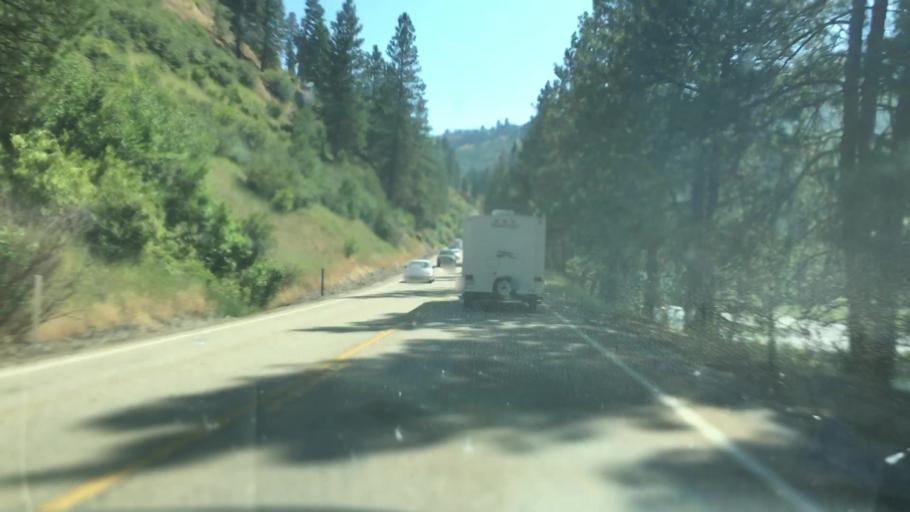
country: US
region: Idaho
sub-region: Boise County
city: Idaho City
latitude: 44.0599
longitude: -116.1252
